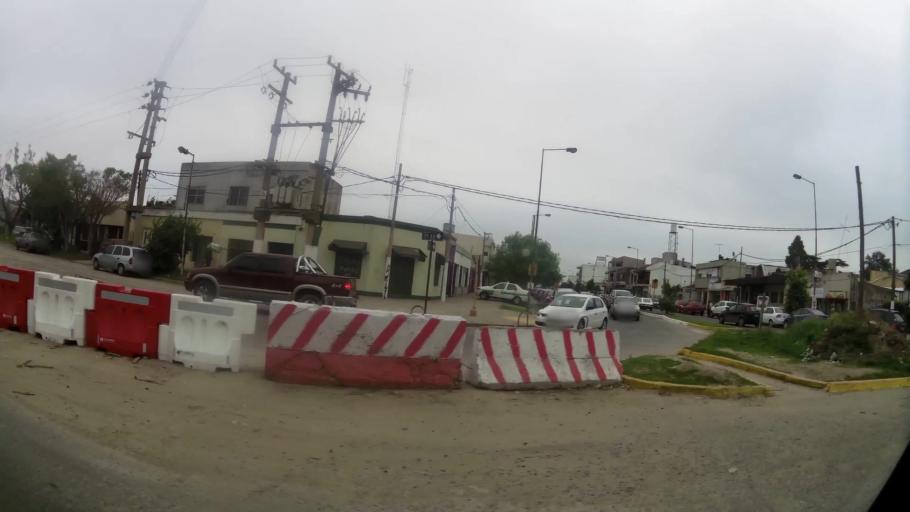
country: AR
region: Buenos Aires
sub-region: Partido de La Plata
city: La Plata
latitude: -34.9235
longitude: -57.9940
